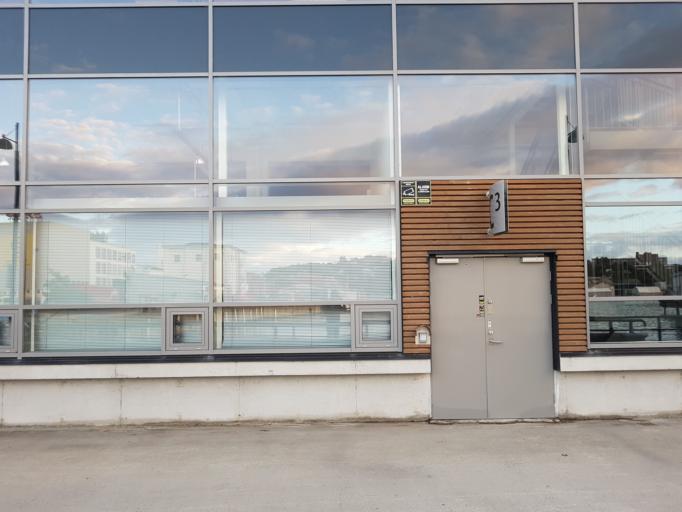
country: NO
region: Sor-Trondelag
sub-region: Trondheim
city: Trondheim
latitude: 63.4401
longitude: 10.4228
